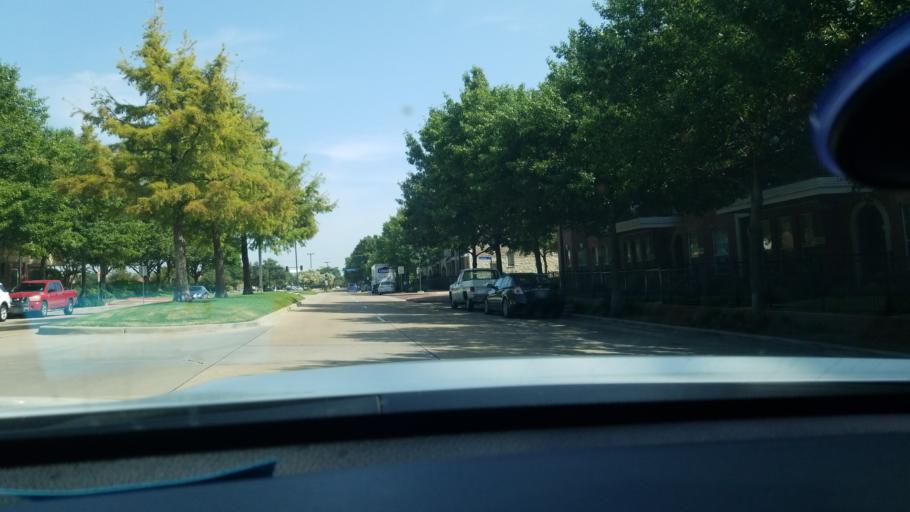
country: US
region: Texas
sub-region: Dallas County
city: Addison
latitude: 32.9643
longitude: -96.8257
